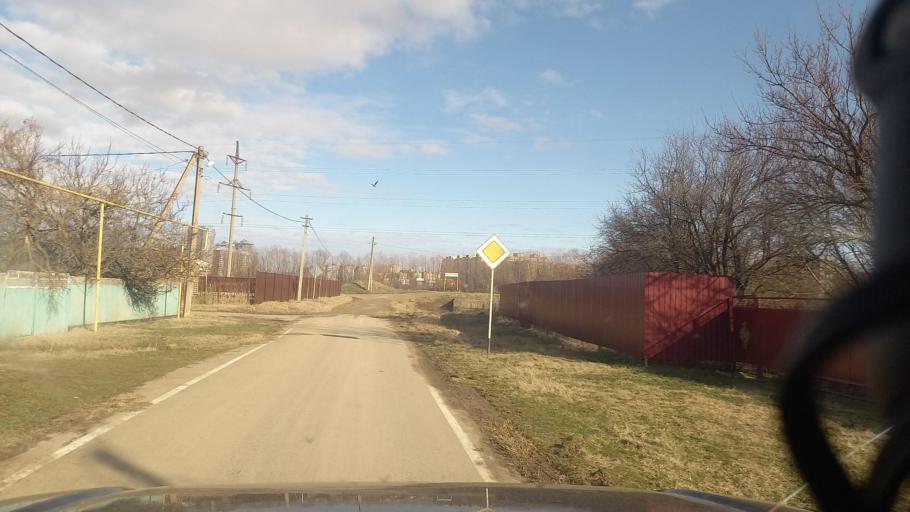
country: RU
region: Adygeya
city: Yablonovskiy
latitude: 45.0342
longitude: 38.8974
